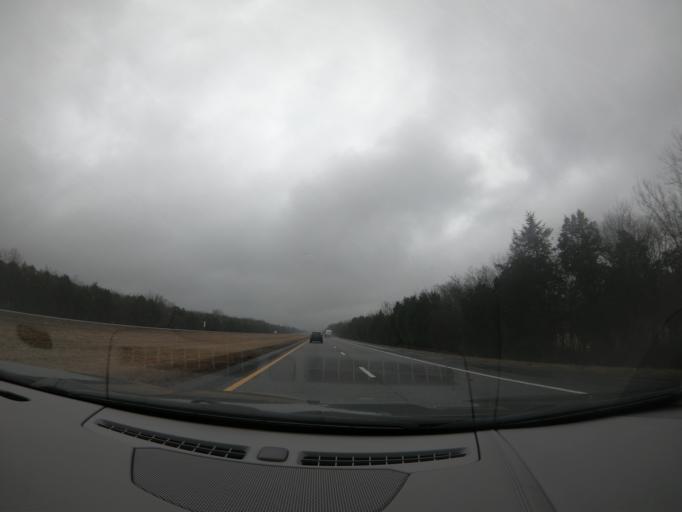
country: US
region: Tennessee
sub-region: Rutherford County
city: Plainview
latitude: 35.6811
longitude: -86.2890
